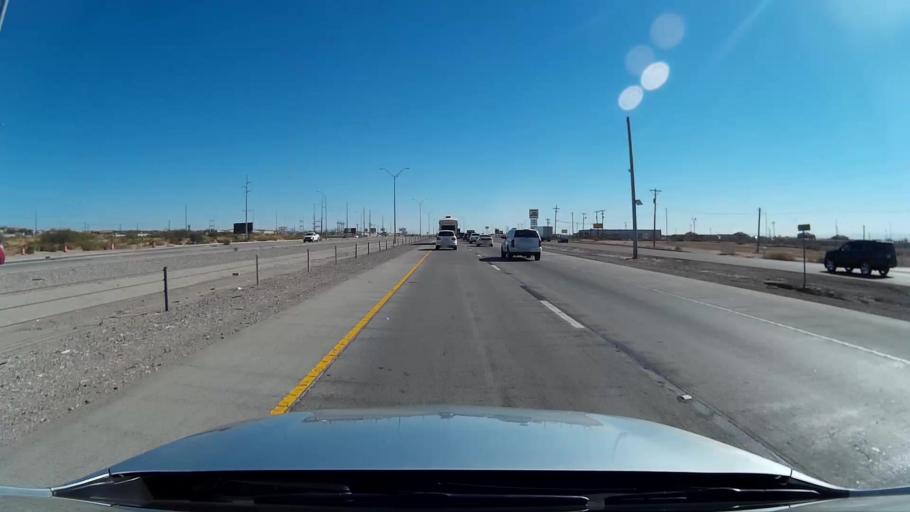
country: US
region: Texas
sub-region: El Paso County
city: Sparks
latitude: 31.6741
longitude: -106.2537
